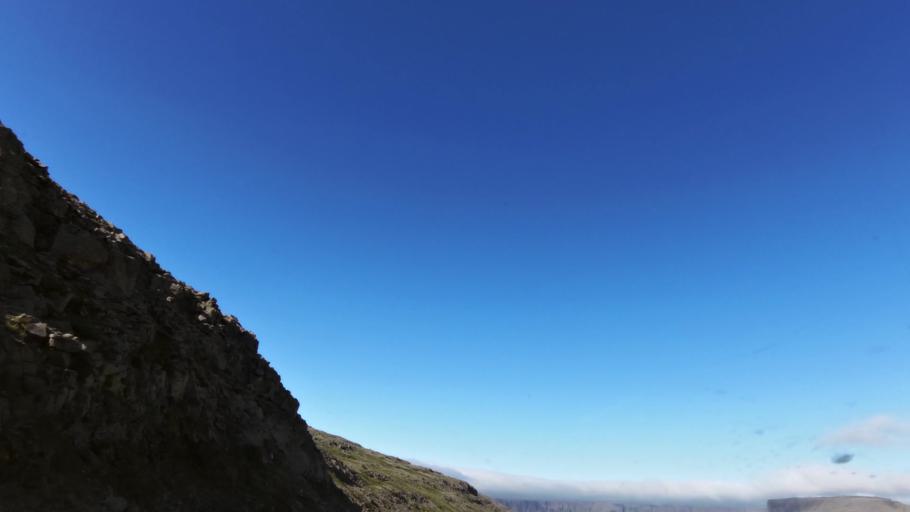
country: IS
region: West
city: Olafsvik
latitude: 65.5551
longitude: -24.1970
